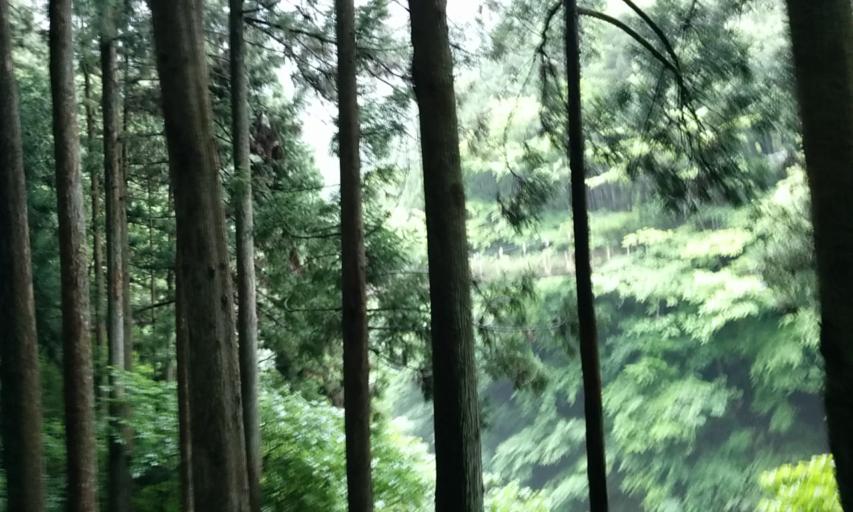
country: JP
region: Tokyo
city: Itsukaichi
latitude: 35.7930
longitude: 139.0604
